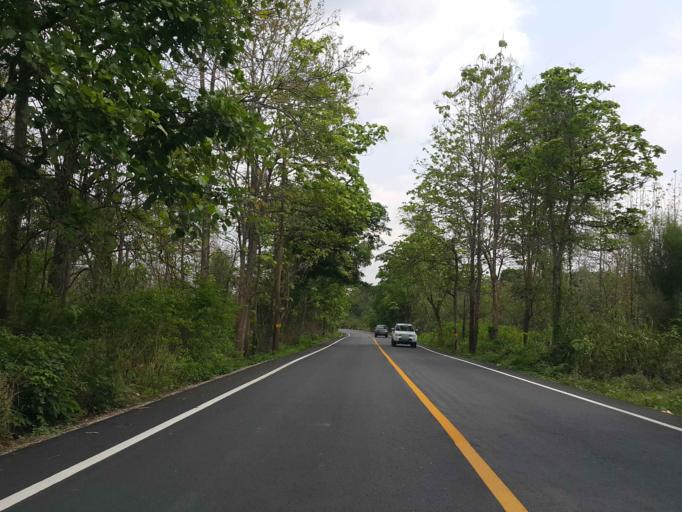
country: TH
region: Lampang
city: Thoen
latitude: 17.5607
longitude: 99.3332
